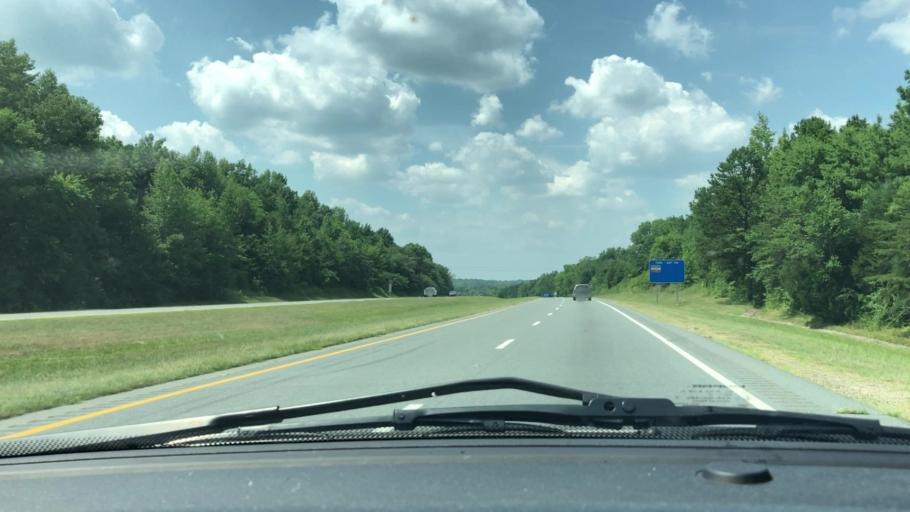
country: US
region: North Carolina
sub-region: Guilford County
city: Forest Oaks
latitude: 35.9502
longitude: -79.6905
